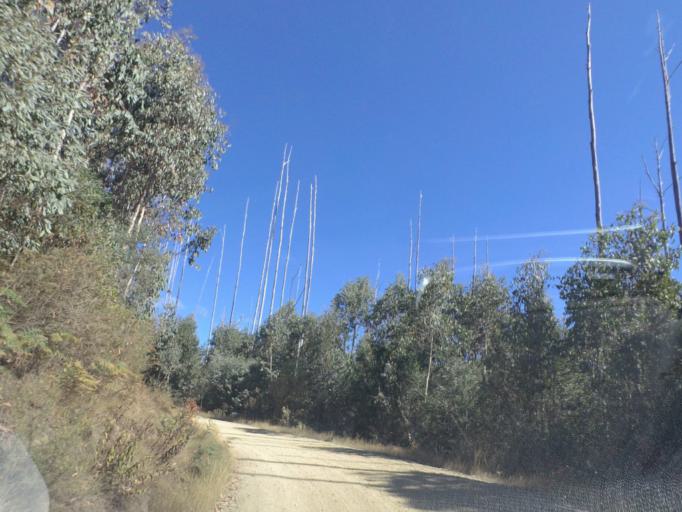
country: AU
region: Victoria
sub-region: Murrindindi
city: Alexandra
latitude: -37.4160
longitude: 145.7996
